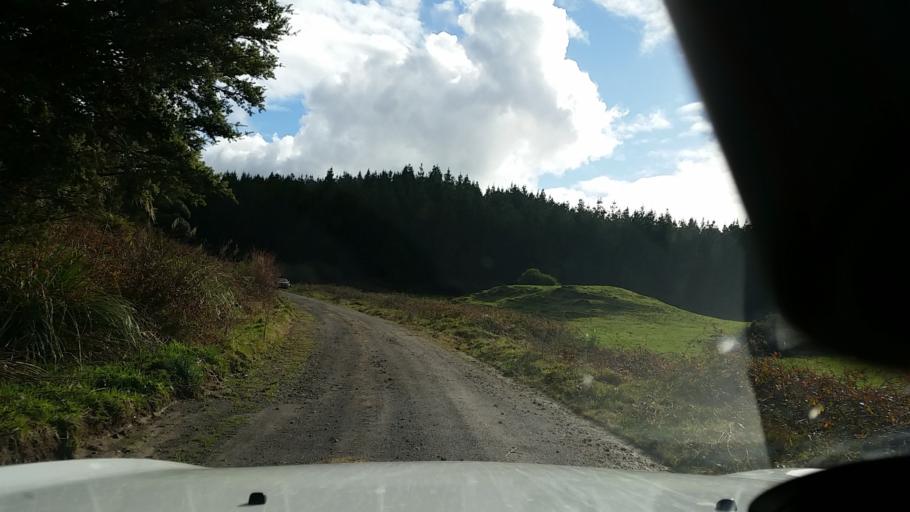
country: NZ
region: Bay of Plenty
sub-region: Rotorua District
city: Rotorua
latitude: -38.0751
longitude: 176.0358
